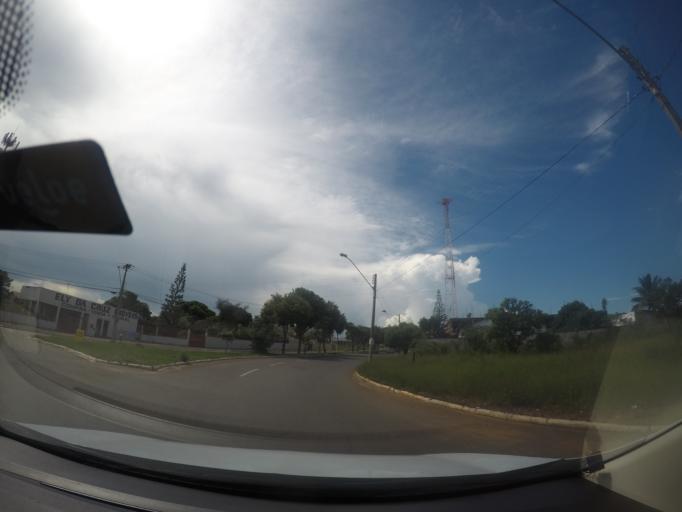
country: BR
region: Goias
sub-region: Trindade
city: Trindade
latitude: -16.6580
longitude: -49.3852
